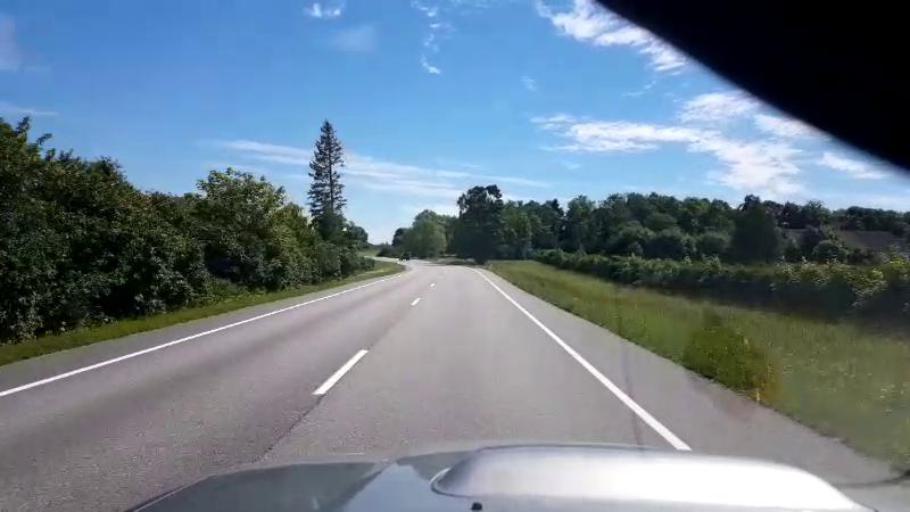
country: EE
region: Jaervamaa
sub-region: Jaerva-Jaani vald
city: Jarva-Jaani
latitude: 59.0040
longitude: 25.9311
